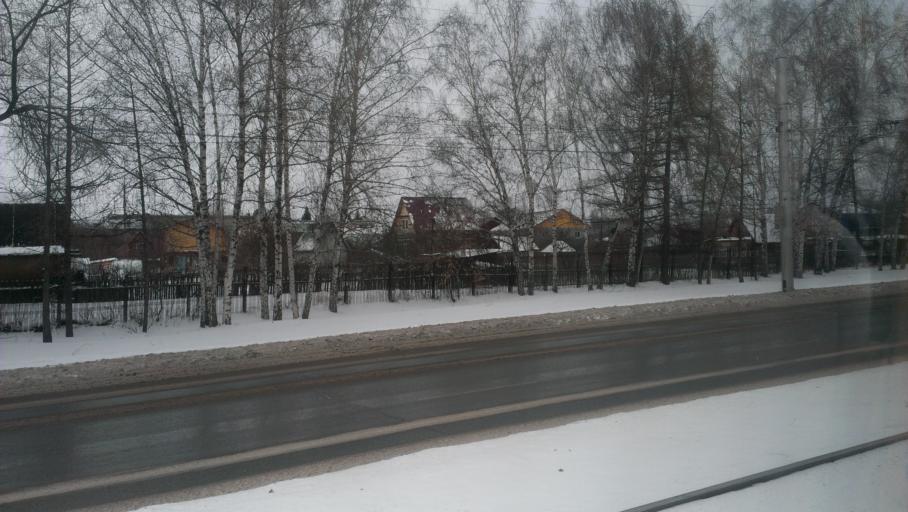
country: RU
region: Altai Krai
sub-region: Gorod Barnaulskiy
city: Barnaul
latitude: 53.3808
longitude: 83.7131
